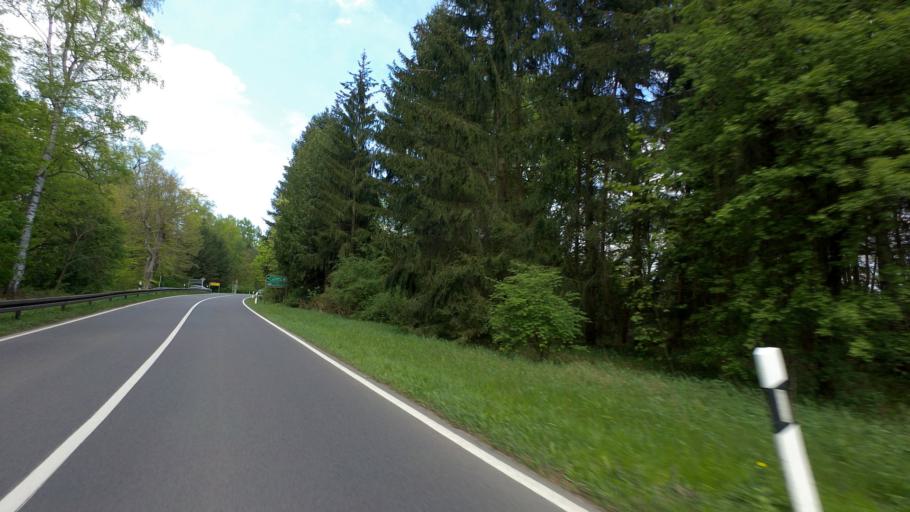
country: DE
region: Brandenburg
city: Friedrichswalde
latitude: 53.0003
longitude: 13.5959
